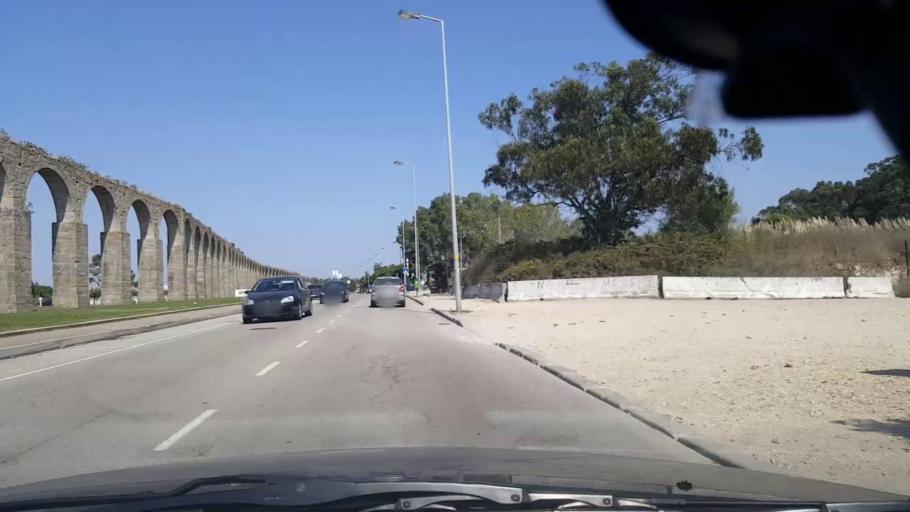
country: PT
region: Porto
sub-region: Vila do Conde
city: Vila do Conde
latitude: 41.3638
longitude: -8.7415
